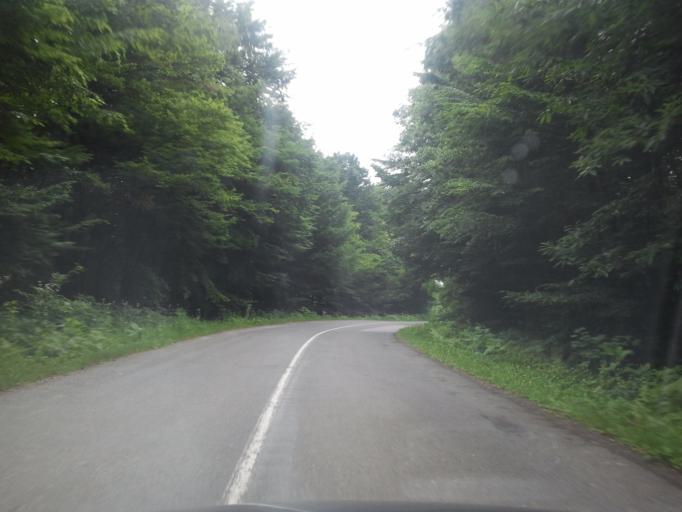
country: HR
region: Sisacko-Moslavacka
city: Gvozd
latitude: 45.3783
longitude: 15.9148
